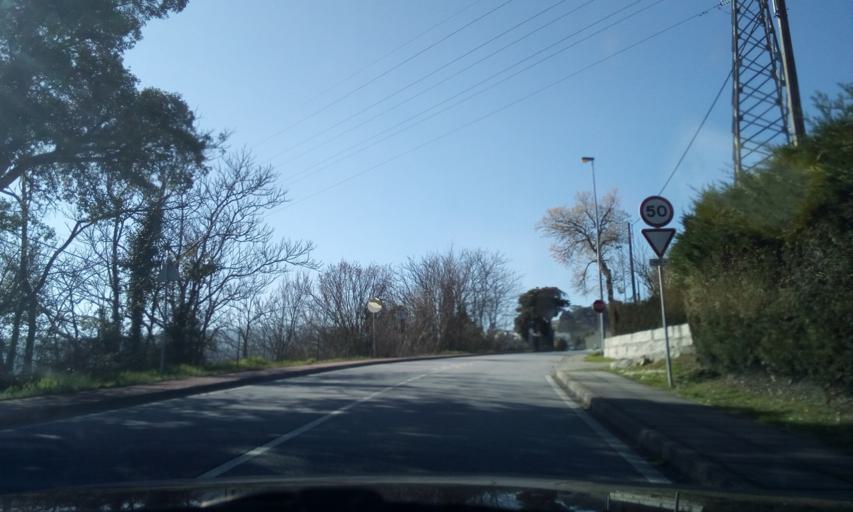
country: PT
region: Guarda
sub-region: Celorico da Beira
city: Celorico da Beira
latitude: 40.6465
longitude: -7.3838
